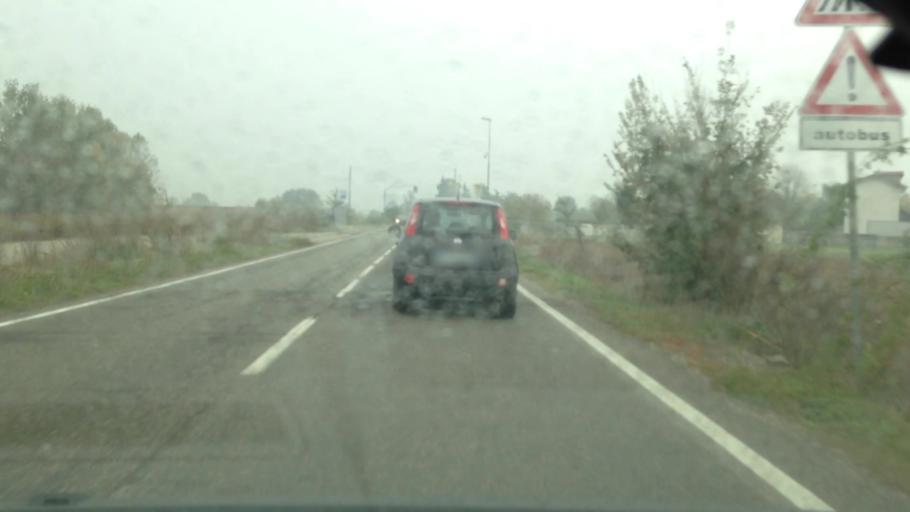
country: IT
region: Piedmont
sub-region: Provincia di Alessandria
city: Felizzano
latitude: 44.9042
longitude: 8.4572
